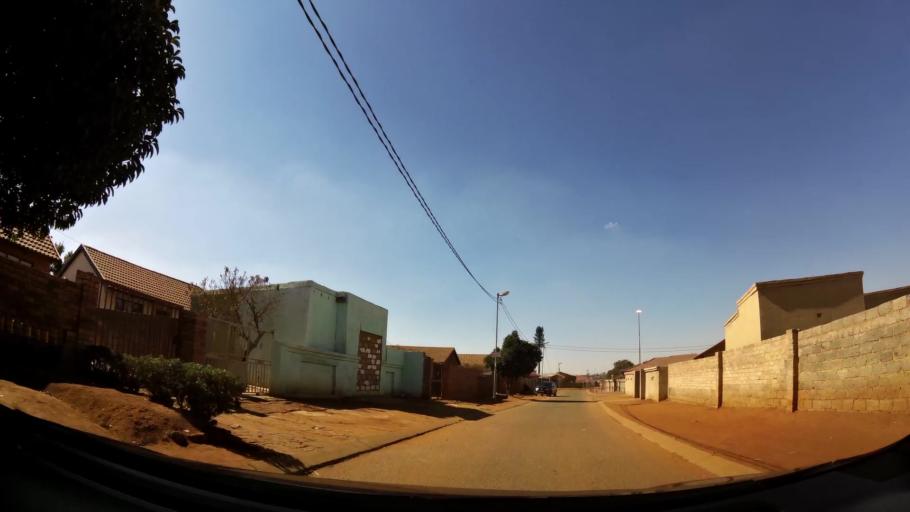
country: ZA
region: Gauteng
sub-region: City of Johannesburg Metropolitan Municipality
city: Soweto
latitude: -26.2429
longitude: 27.8057
